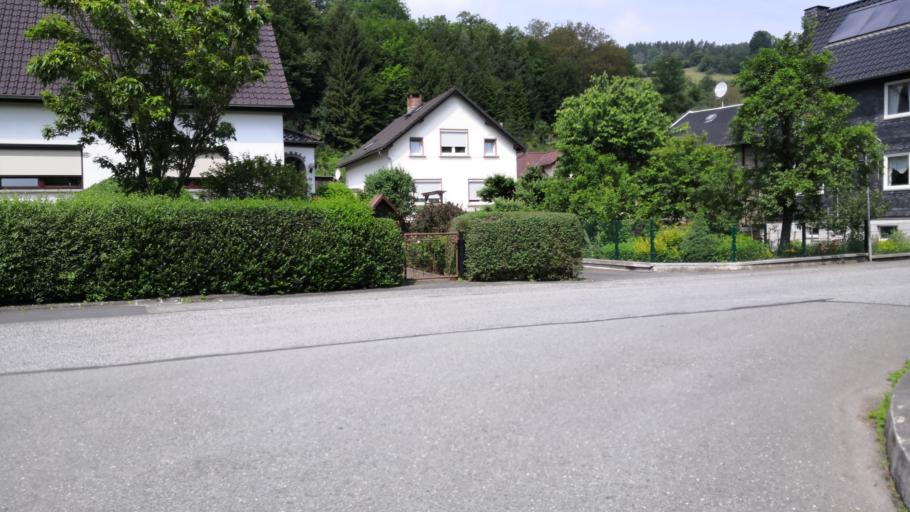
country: DE
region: Thuringia
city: Probstzella
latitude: 50.5627
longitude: 11.3472
